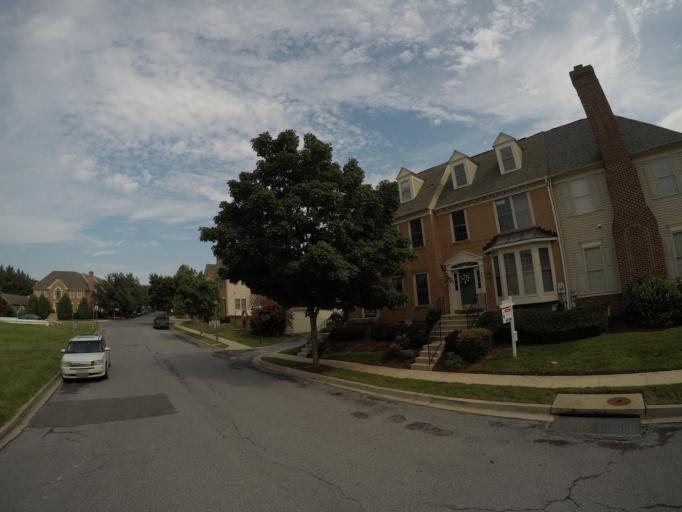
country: US
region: Maryland
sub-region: Frederick County
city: Clover Hill
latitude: 39.4550
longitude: -77.3843
